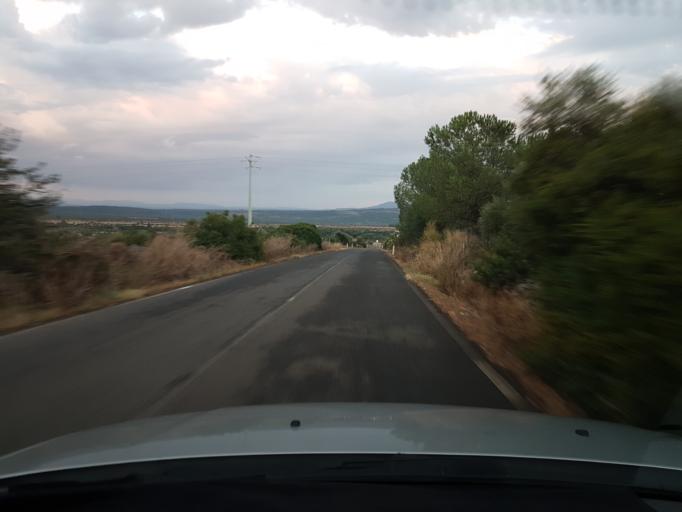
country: IT
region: Sardinia
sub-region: Provincia di Oristano
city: Milis
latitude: 40.0575
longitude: 8.6354
